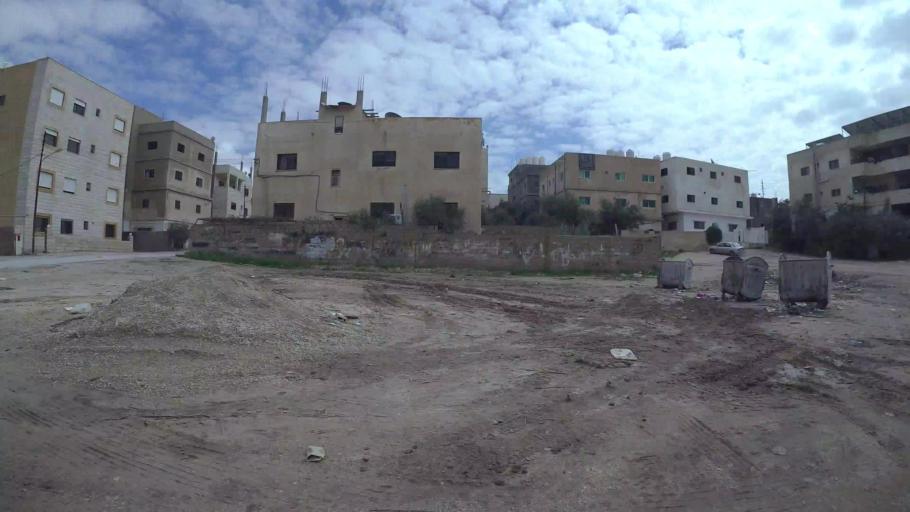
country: JO
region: Amman
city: Al Jubayhah
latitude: 32.0612
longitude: 35.8291
